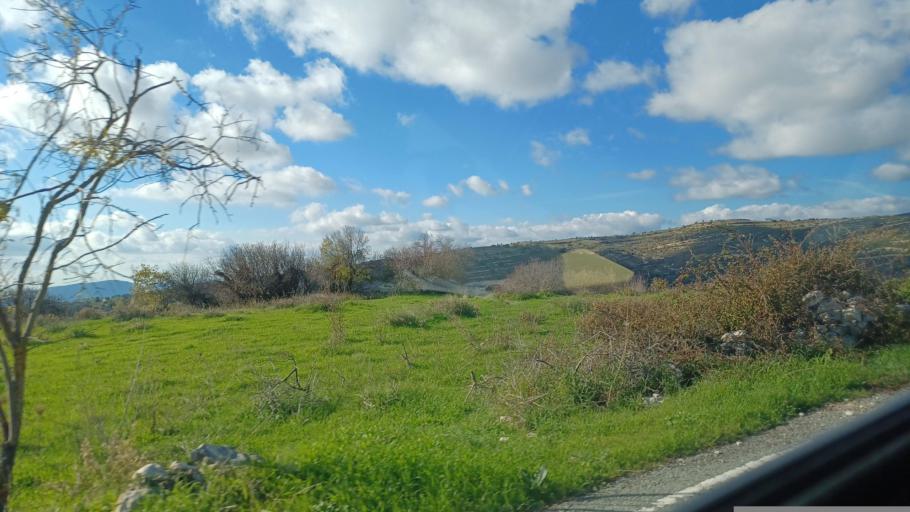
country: CY
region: Limassol
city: Pachna
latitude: 34.8360
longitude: 32.7993
